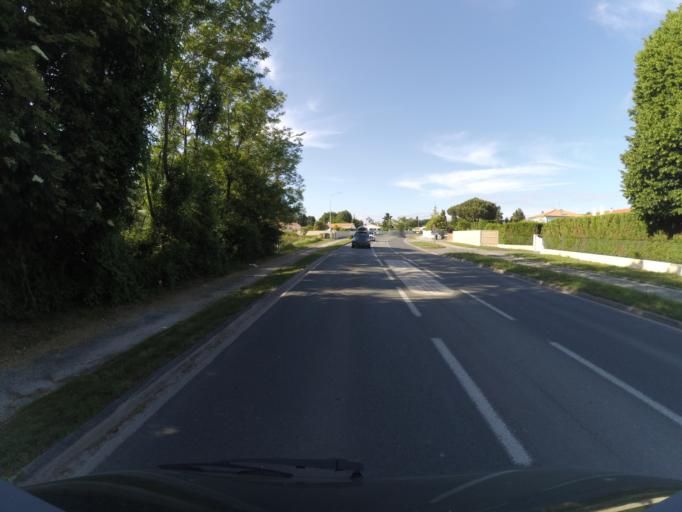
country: FR
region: Poitou-Charentes
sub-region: Departement de la Charente-Maritime
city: Saint-Sulpice-de-Royan
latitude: 45.6562
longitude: -1.0231
